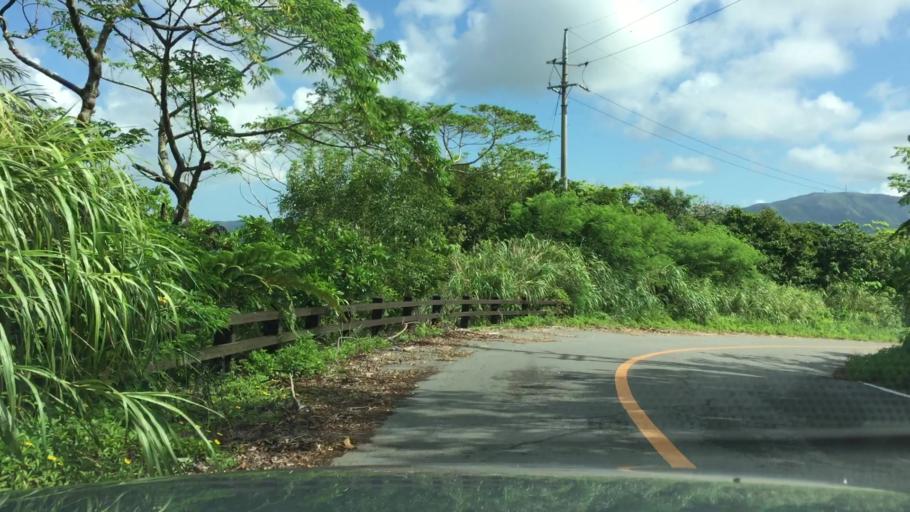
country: JP
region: Okinawa
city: Ishigaki
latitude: 24.3818
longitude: 124.1653
